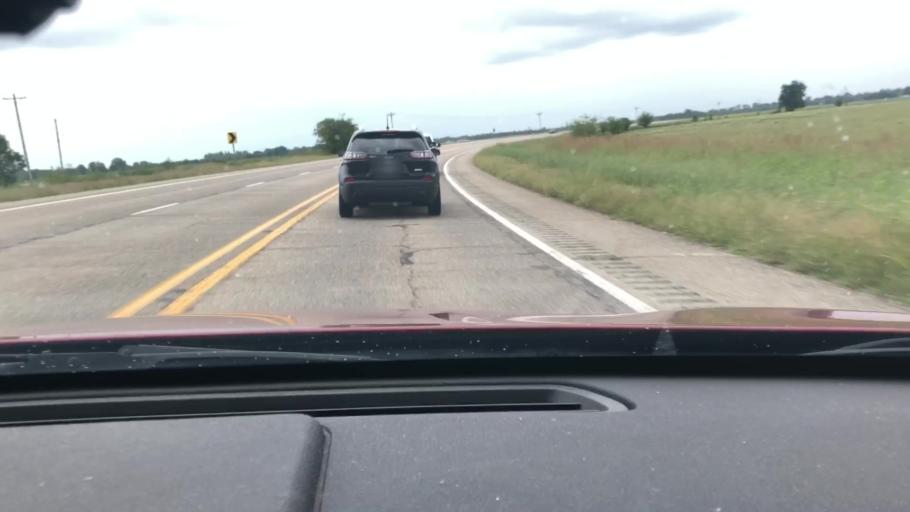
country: US
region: Arkansas
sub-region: Lafayette County
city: Lewisville
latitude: 33.3921
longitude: -93.7374
